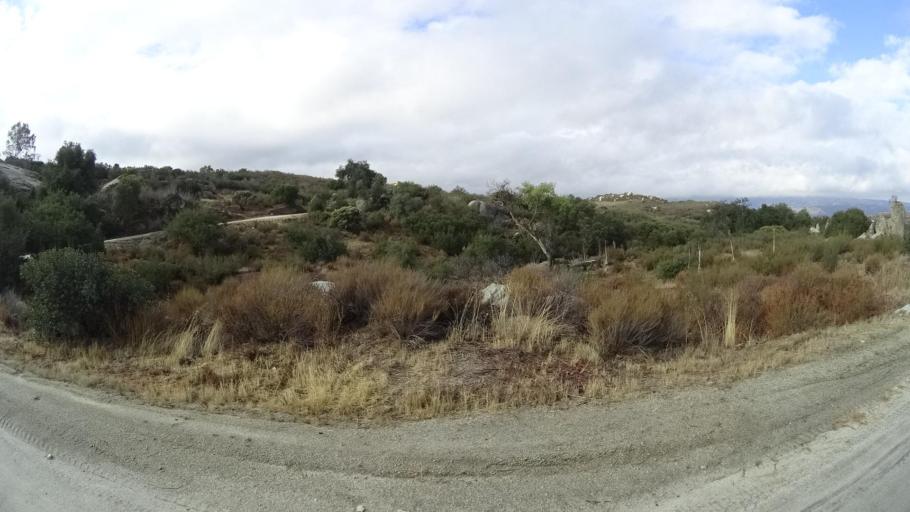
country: MX
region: Baja California
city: Tecate
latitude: 32.6427
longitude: -116.6351
